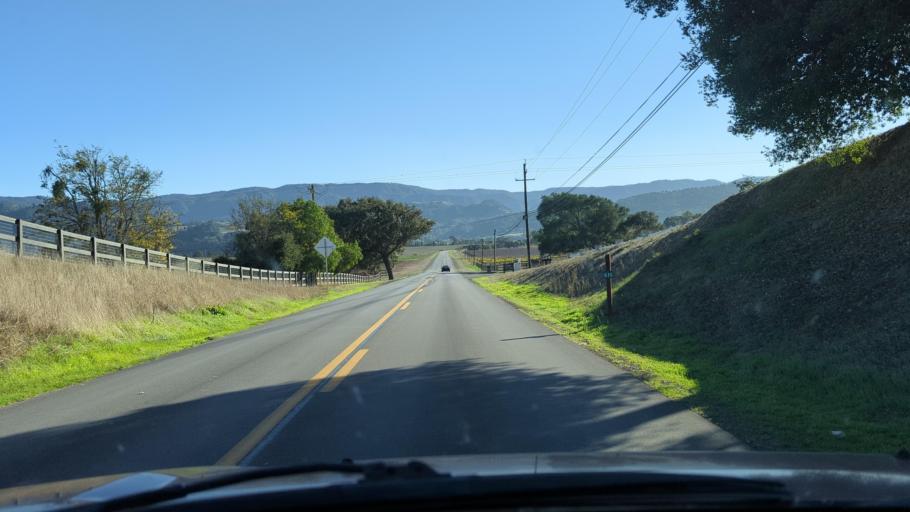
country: US
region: California
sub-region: Santa Barbara County
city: Santa Ynez
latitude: 34.6002
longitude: -120.0982
